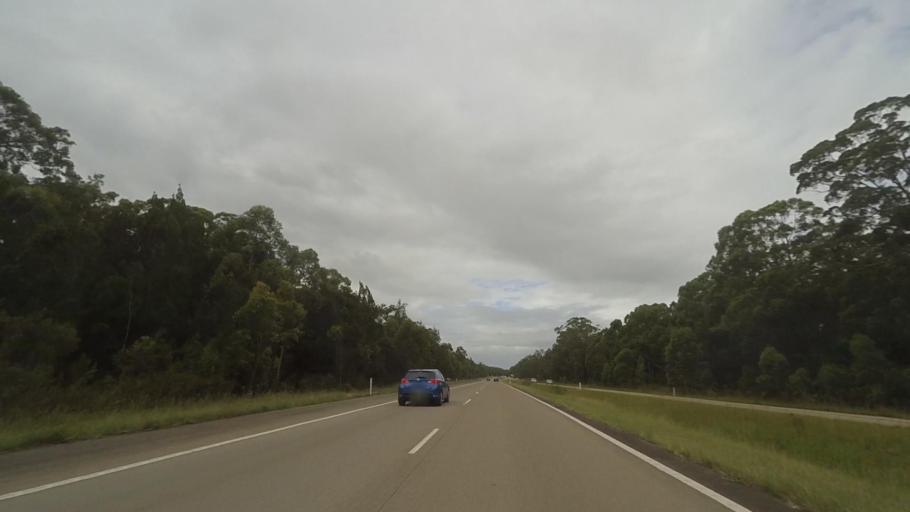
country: AU
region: New South Wales
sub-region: Port Stephens Shire
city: Medowie
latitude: -32.6512
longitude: 151.8941
